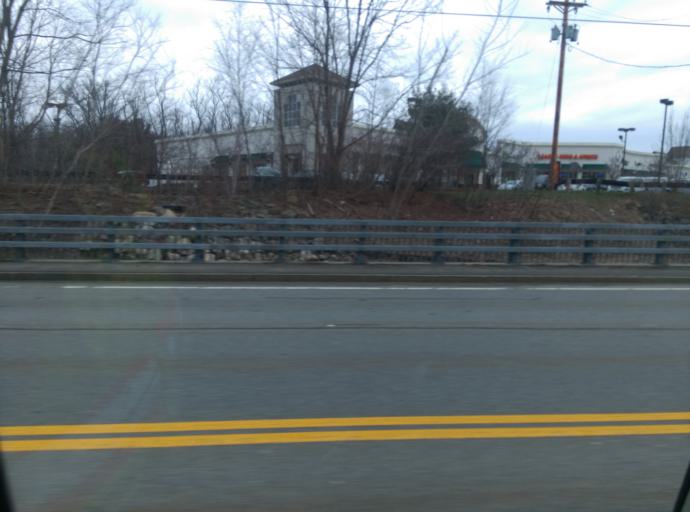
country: US
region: Massachusetts
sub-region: Essex County
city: Amesbury
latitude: 42.8464
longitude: -70.9121
